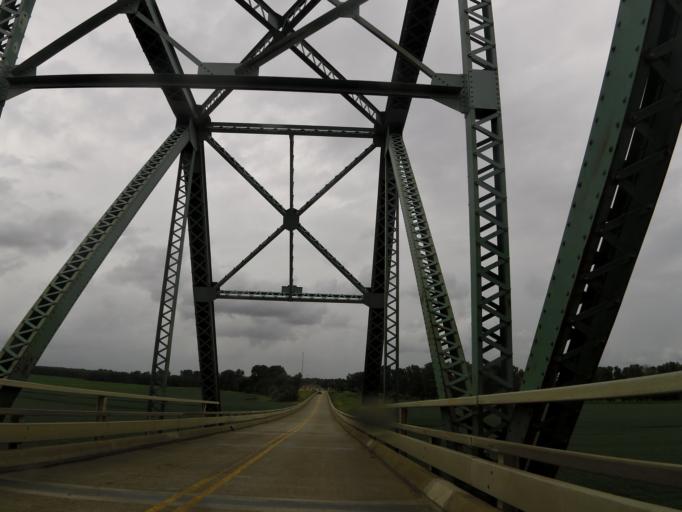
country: US
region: Illinois
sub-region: Alexander County
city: Cairo
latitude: 36.9826
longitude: -89.1493
